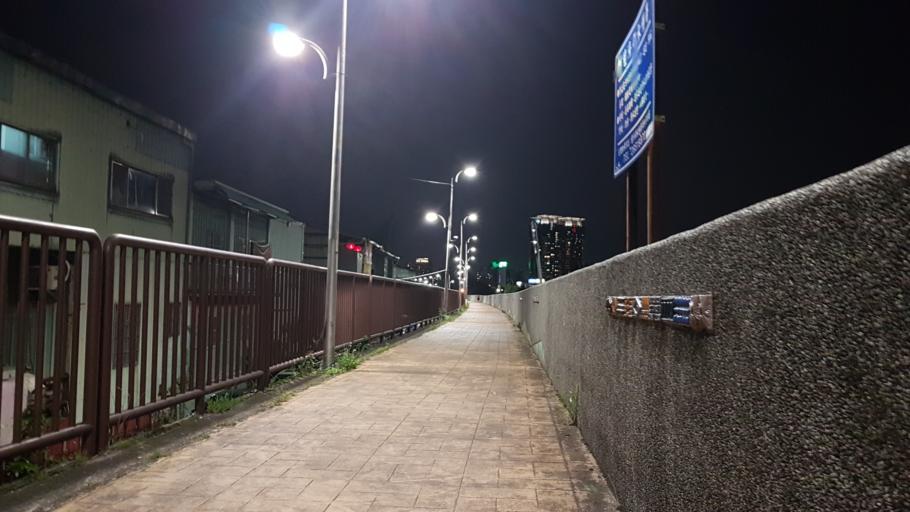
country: TW
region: Taipei
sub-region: Taipei
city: Banqiao
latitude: 24.9626
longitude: 121.5340
